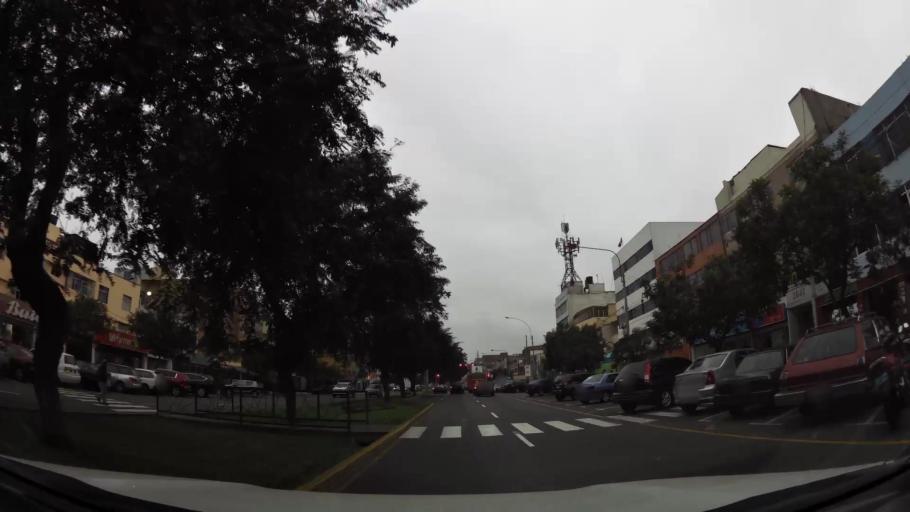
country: PE
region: Lima
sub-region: Lima
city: San Luis
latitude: -12.0907
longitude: -76.9960
